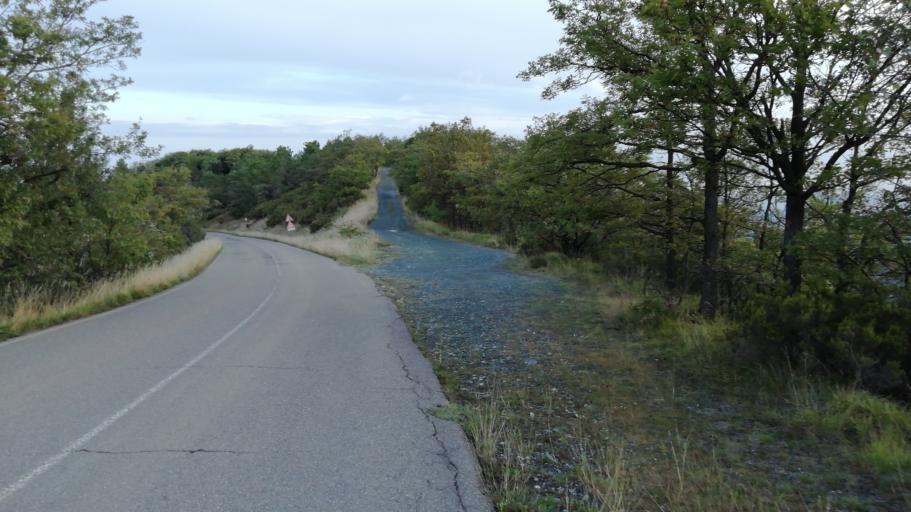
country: IT
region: Piedmont
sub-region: Provincia di Alessandria
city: Bosio
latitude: 44.6224
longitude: 8.7906
